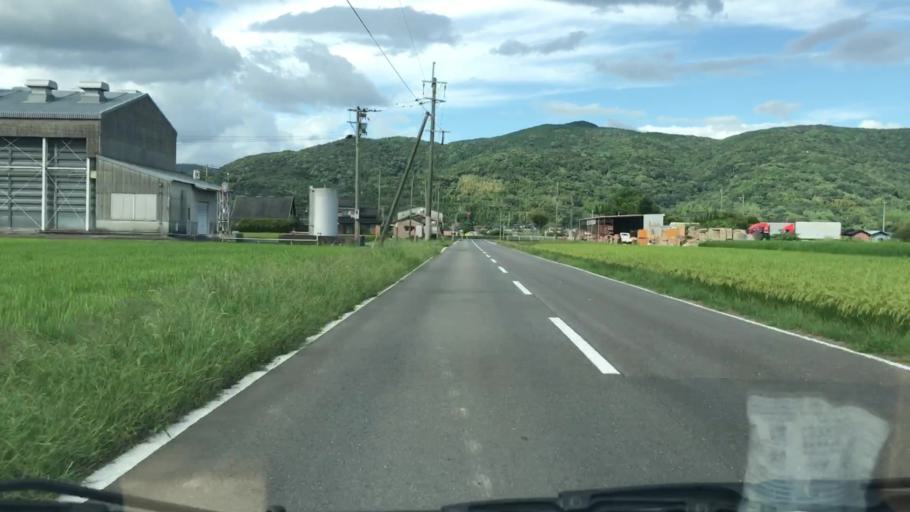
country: JP
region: Saga Prefecture
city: Kashima
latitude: 33.1226
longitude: 130.0724
